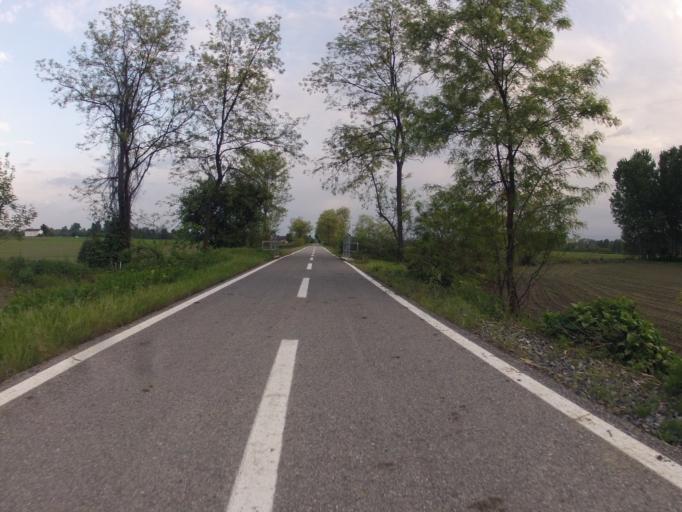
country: IT
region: Piedmont
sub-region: Provincia di Torino
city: Vigone
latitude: 44.8221
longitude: 7.4960
